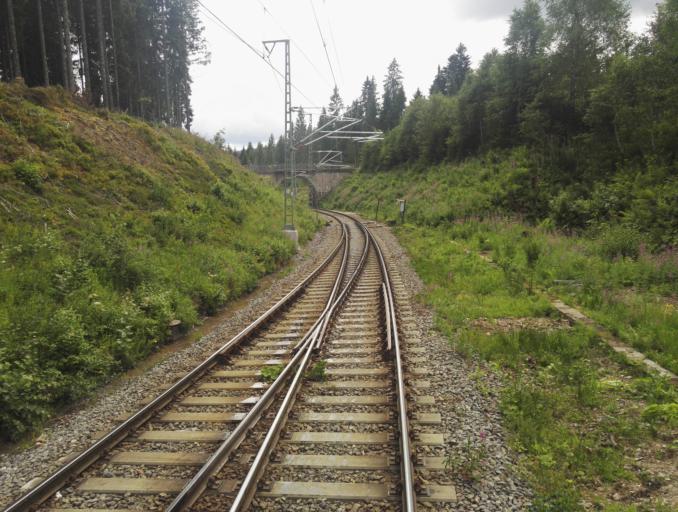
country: DE
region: Baden-Wuerttemberg
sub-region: Freiburg Region
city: Hinterzarten
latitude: 47.8691
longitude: 8.0972
